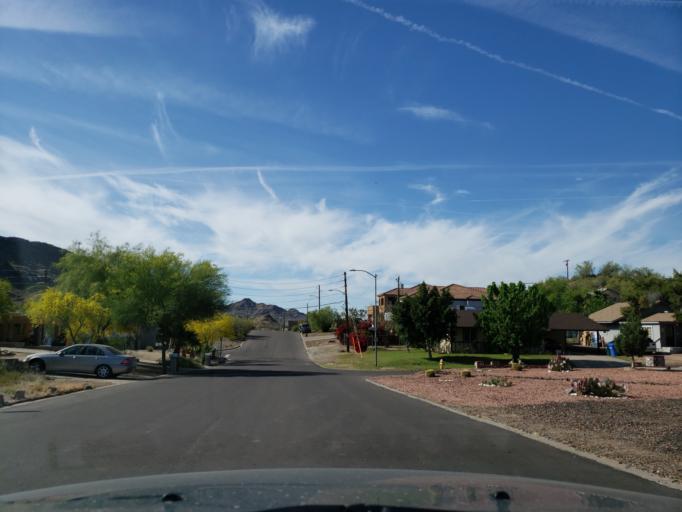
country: US
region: Arizona
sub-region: Maricopa County
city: Paradise Valley
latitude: 33.5913
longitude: -112.0478
